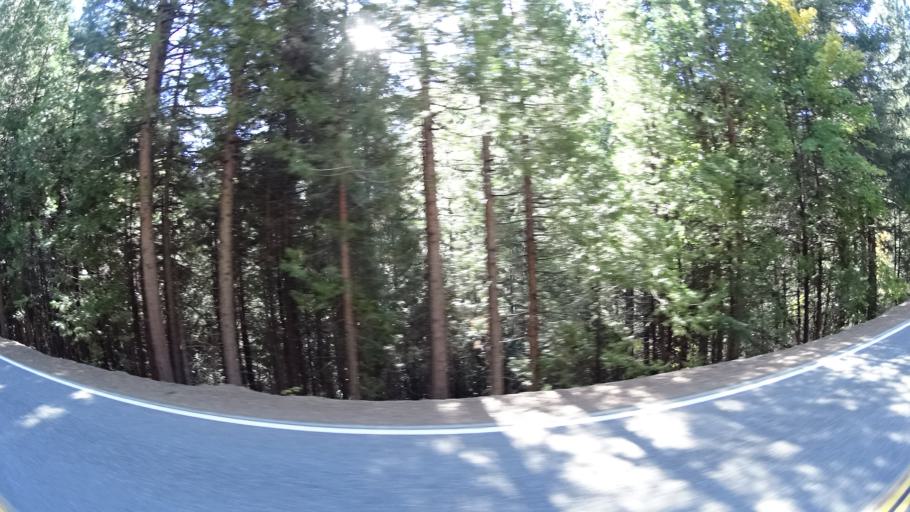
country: US
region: California
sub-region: Trinity County
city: Weaverville
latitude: 41.2256
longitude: -123.0052
